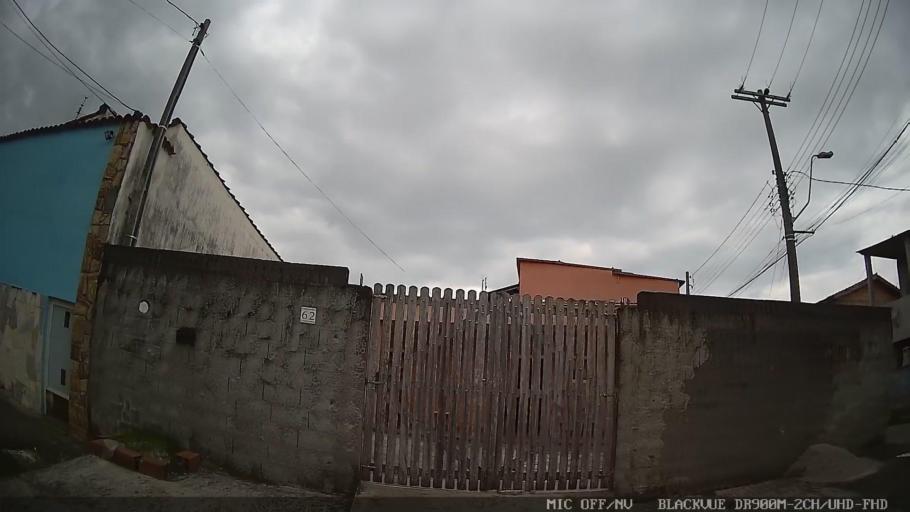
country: BR
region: Sao Paulo
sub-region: Caraguatatuba
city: Caraguatatuba
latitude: -23.6819
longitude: -45.4529
